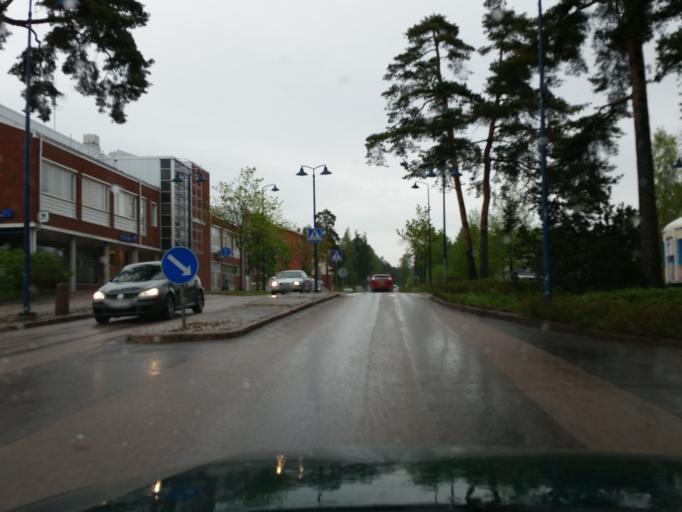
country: FI
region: Uusimaa
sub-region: Helsinki
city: Vihti
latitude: 60.3351
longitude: 24.3208
